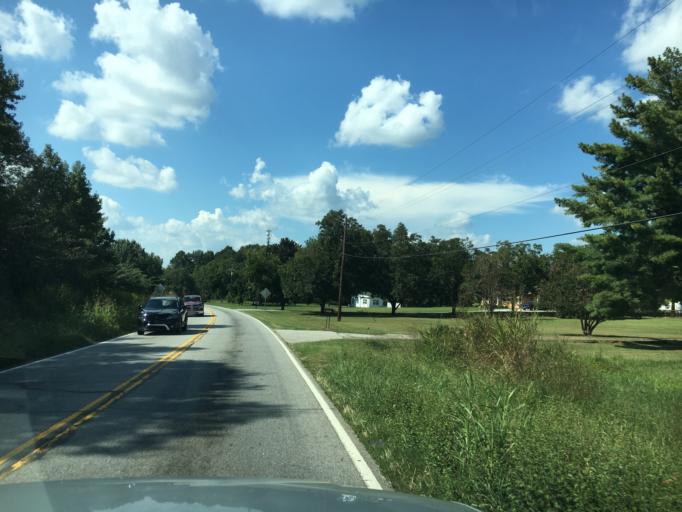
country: US
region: South Carolina
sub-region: Greenville County
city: Fountain Inn
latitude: 34.6337
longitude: -82.1348
